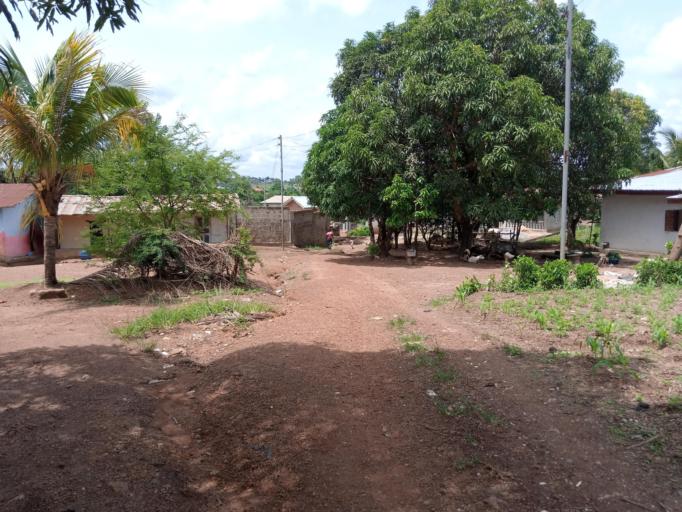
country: SL
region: Southern Province
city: Bo
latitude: 7.9426
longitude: -11.7196
